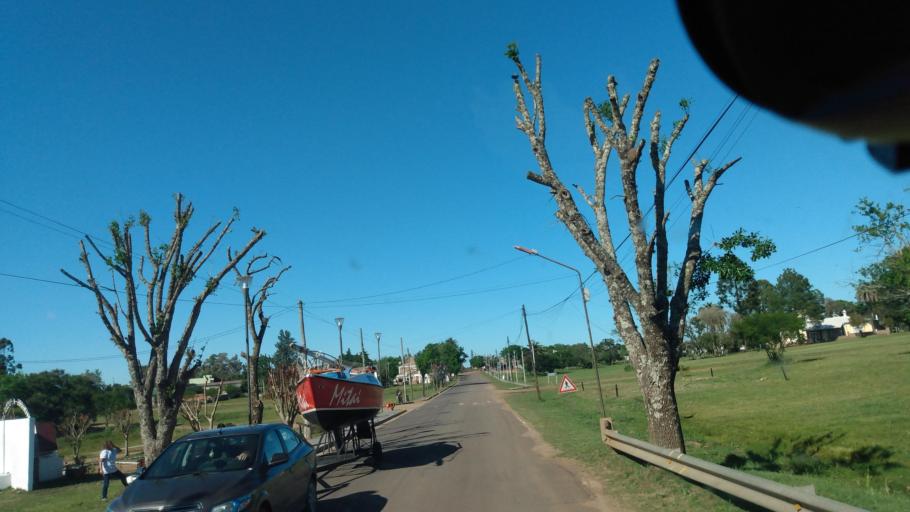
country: AR
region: Entre Rios
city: Colon
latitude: -32.1556
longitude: -58.1961
